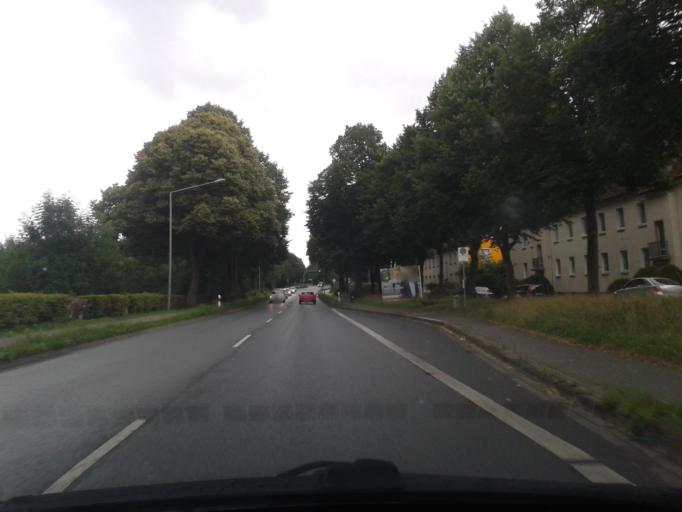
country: DE
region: North Rhine-Westphalia
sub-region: Regierungsbezirk Detmold
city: Detmold
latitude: 51.9290
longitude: 8.8878
